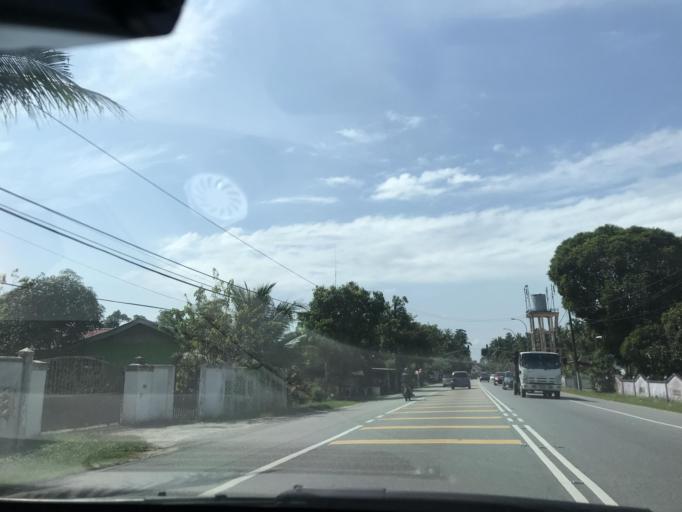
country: MY
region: Kelantan
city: Tumpat
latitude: 6.1378
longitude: 102.1712
